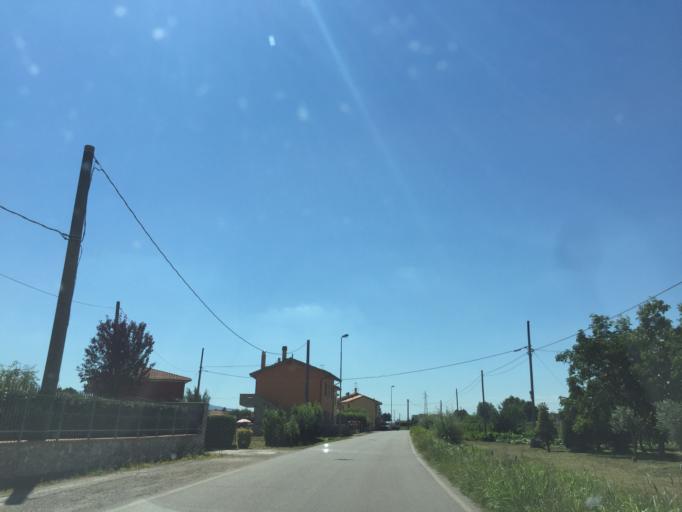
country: IT
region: Tuscany
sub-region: Provincia di Pistoia
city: Ponte Buggianese
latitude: 43.8335
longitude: 10.7412
